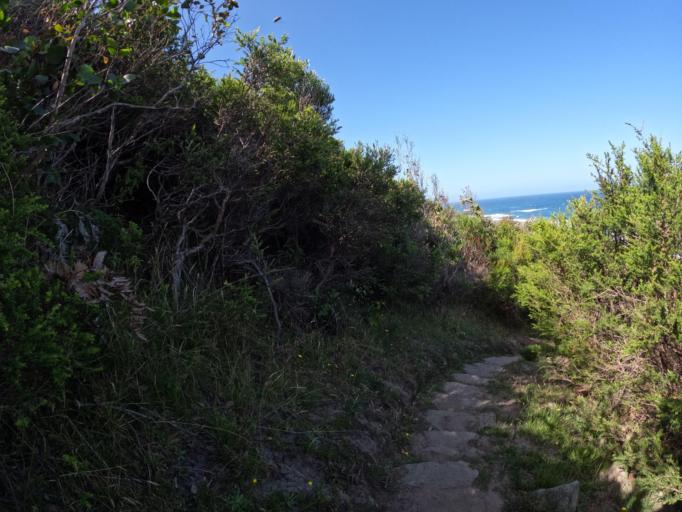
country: AU
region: Victoria
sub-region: Colac-Otway
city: Apollo Bay
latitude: -38.7893
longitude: 143.6481
